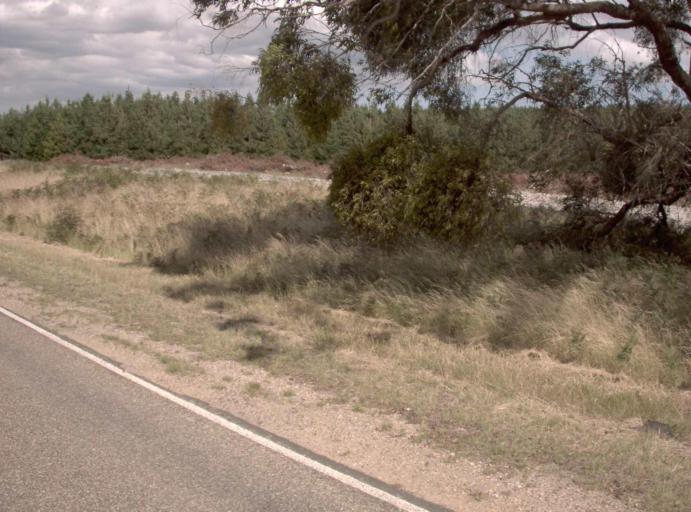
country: AU
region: Victoria
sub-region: Wellington
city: Sale
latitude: -38.1610
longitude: 146.9118
